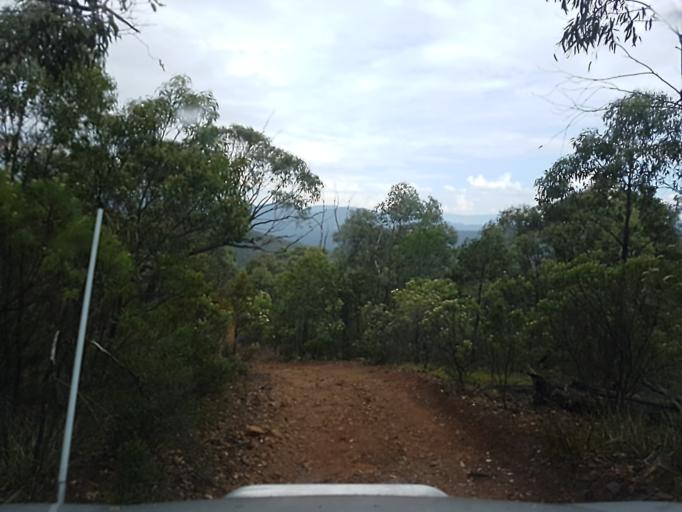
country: AU
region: New South Wales
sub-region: Snowy River
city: Jindabyne
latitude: -36.9252
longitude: 148.3539
